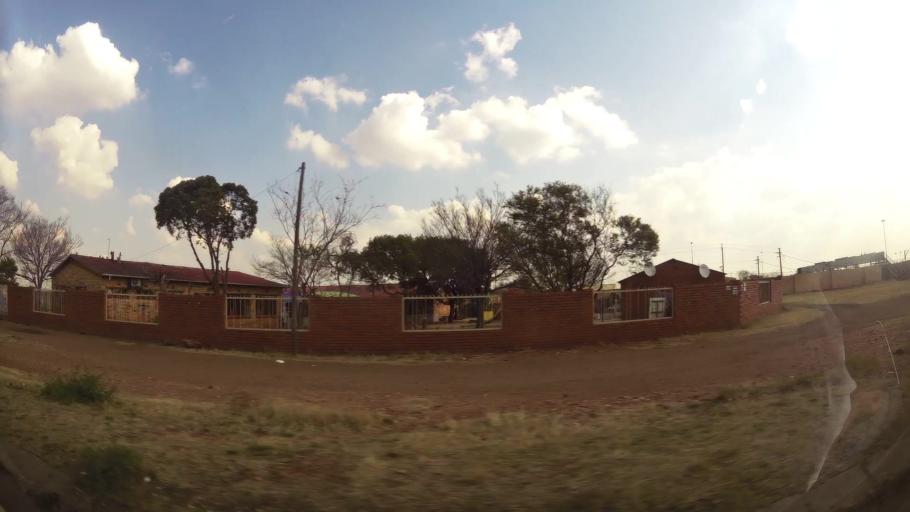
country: ZA
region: Gauteng
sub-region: Ekurhuleni Metropolitan Municipality
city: Germiston
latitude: -26.3419
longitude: 28.1533
